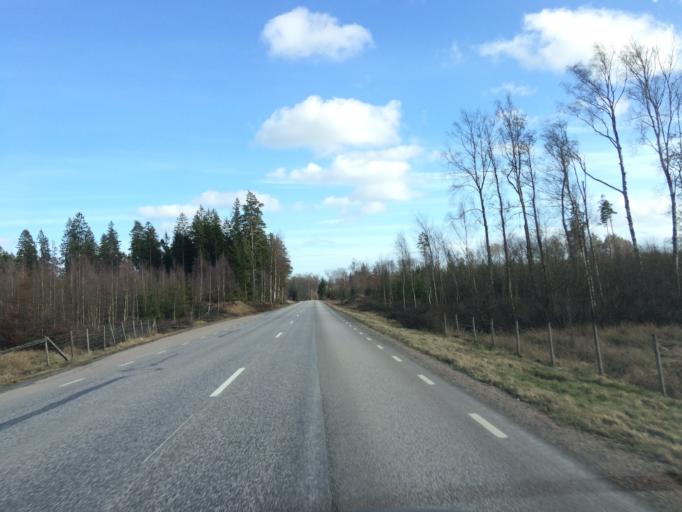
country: SE
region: Kronoberg
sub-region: Almhults Kommun
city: AElmhult
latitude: 56.5774
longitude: 14.1051
